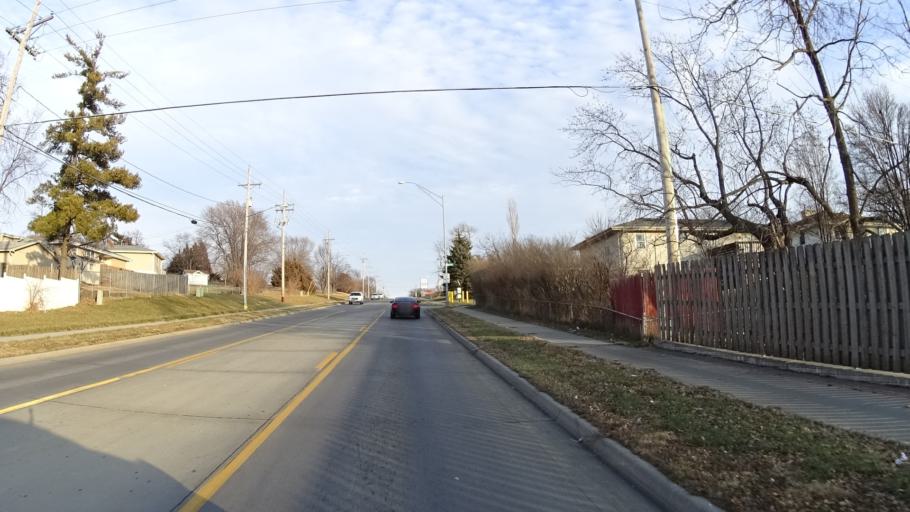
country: US
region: Nebraska
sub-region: Sarpy County
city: La Vista
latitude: 41.1907
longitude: -95.9978
